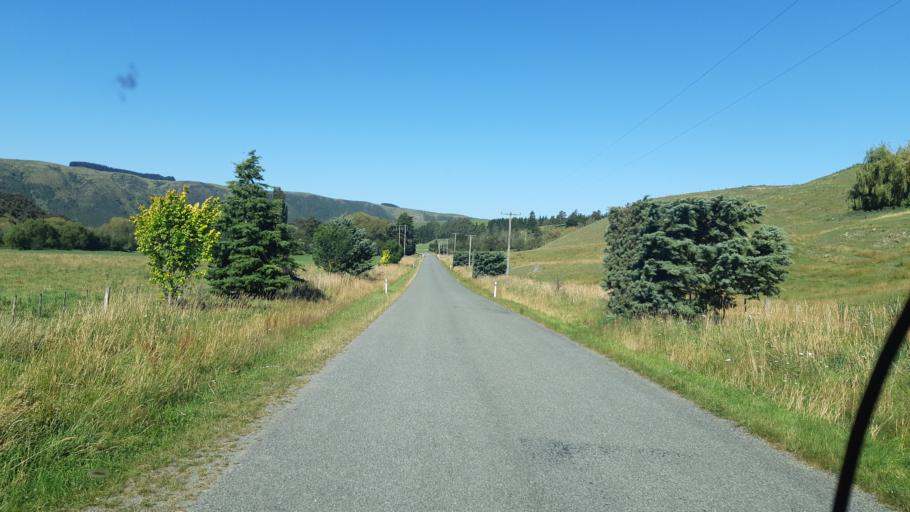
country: NZ
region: Canterbury
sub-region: Timaru District
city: Pleasant Point
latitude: -44.2884
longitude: 170.8875
